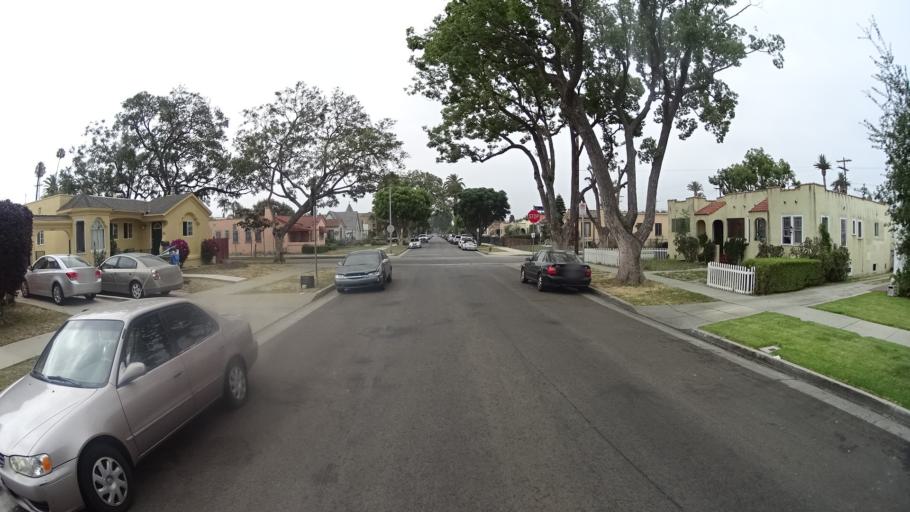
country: US
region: California
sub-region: Los Angeles County
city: View Park-Windsor Hills
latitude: 34.0314
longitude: -118.3384
